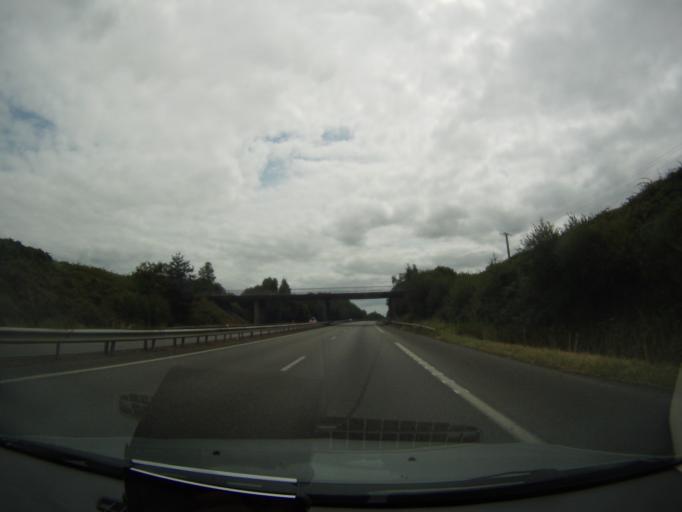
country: FR
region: Pays de la Loire
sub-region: Departement de la Loire-Atlantique
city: Orvault
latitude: 47.2902
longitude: -1.6099
